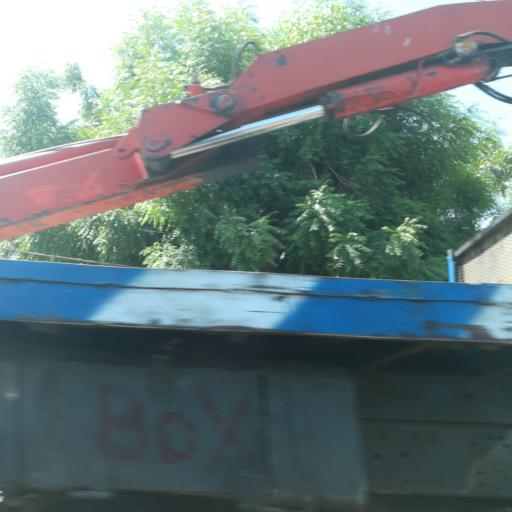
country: NG
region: Kano
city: Kano
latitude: 12.0047
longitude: 8.5379
